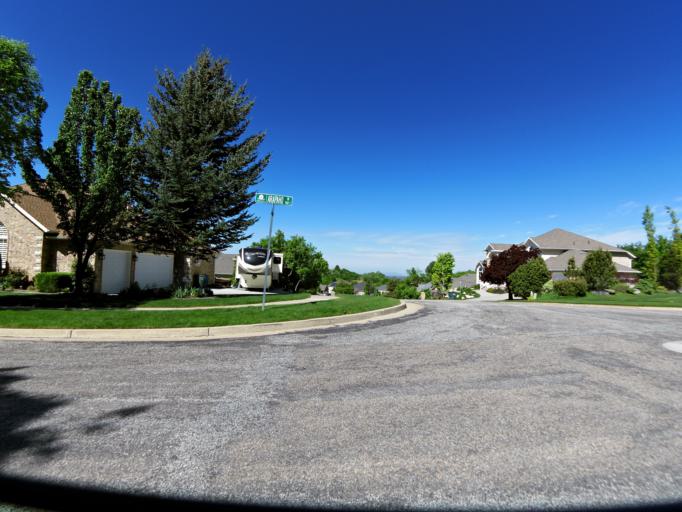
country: US
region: Utah
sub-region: Weber County
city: Uintah
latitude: 41.1678
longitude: -111.9283
